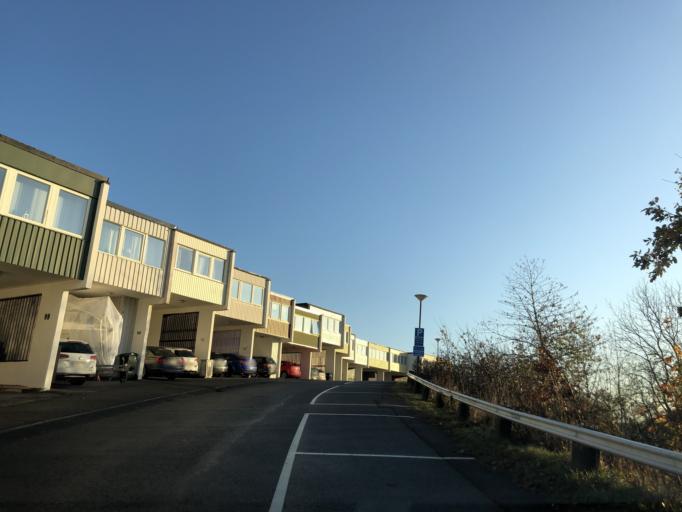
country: SE
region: Vaestra Goetaland
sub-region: Goteborg
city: Hammarkullen
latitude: 57.7778
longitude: 12.0274
